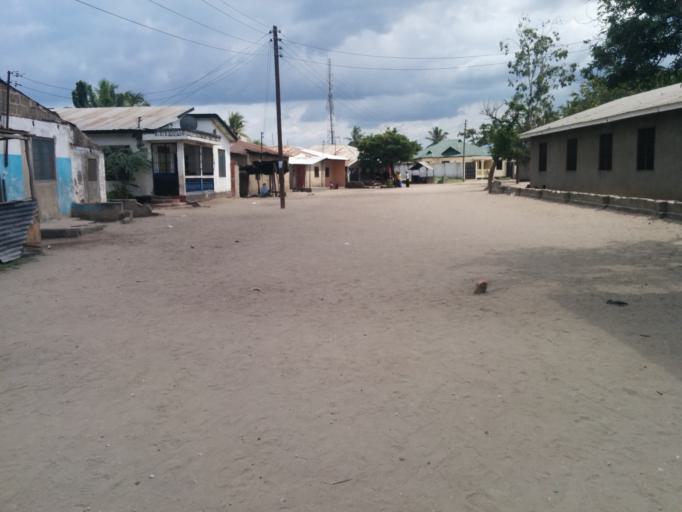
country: TZ
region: Dar es Salaam
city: Dar es Salaam
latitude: -6.8630
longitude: 39.2558
